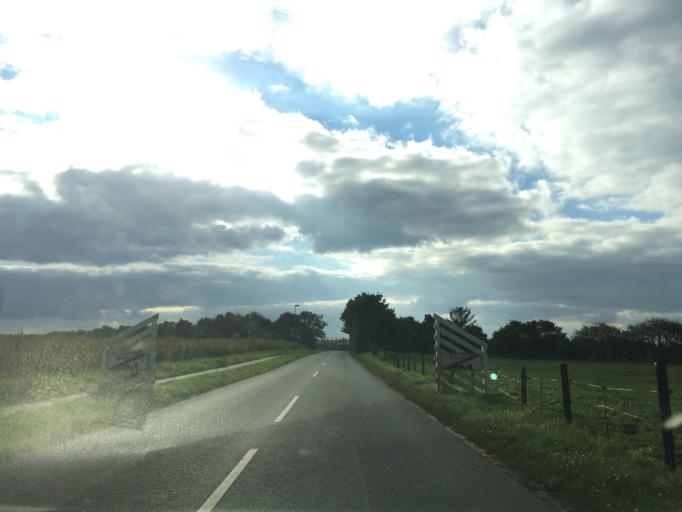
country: DK
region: Central Jutland
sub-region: Favrskov Kommune
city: Ulstrup
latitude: 56.2786
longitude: 9.7414
